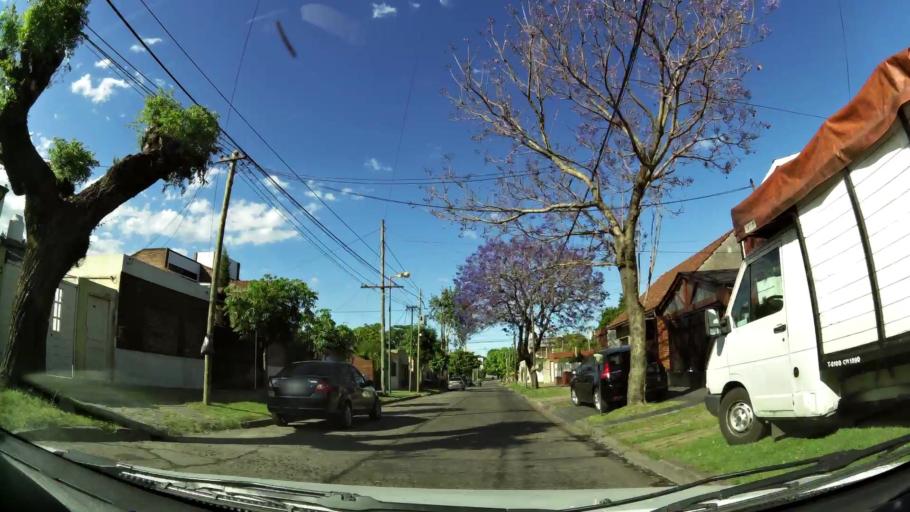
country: AR
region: Buenos Aires
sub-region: Partido de General San Martin
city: General San Martin
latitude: -34.5374
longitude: -58.5647
